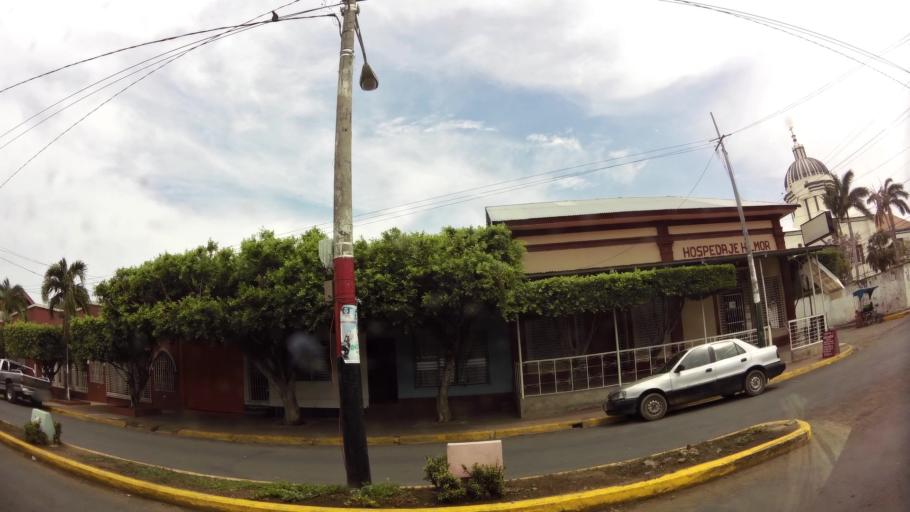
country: NI
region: Rivas
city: Rivas
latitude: 11.4399
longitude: -85.8273
